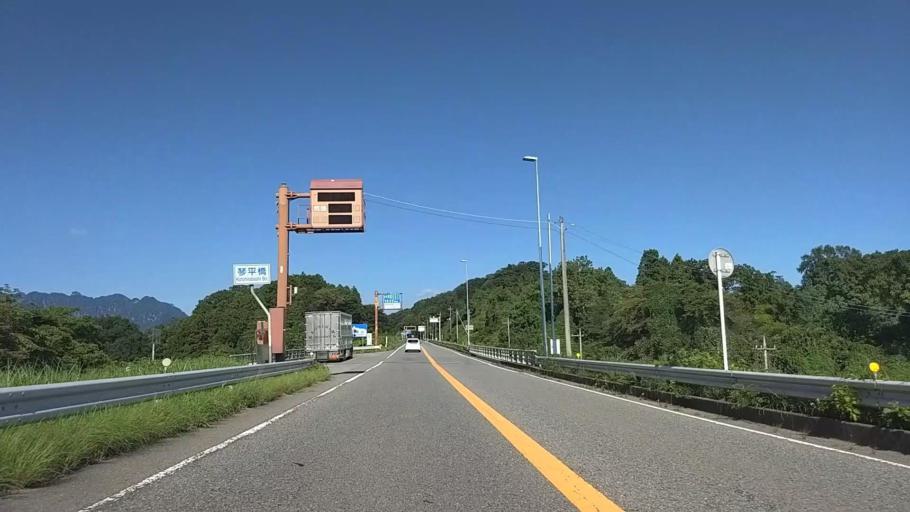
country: JP
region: Gunma
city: Annaka
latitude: 36.3145
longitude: 138.8073
